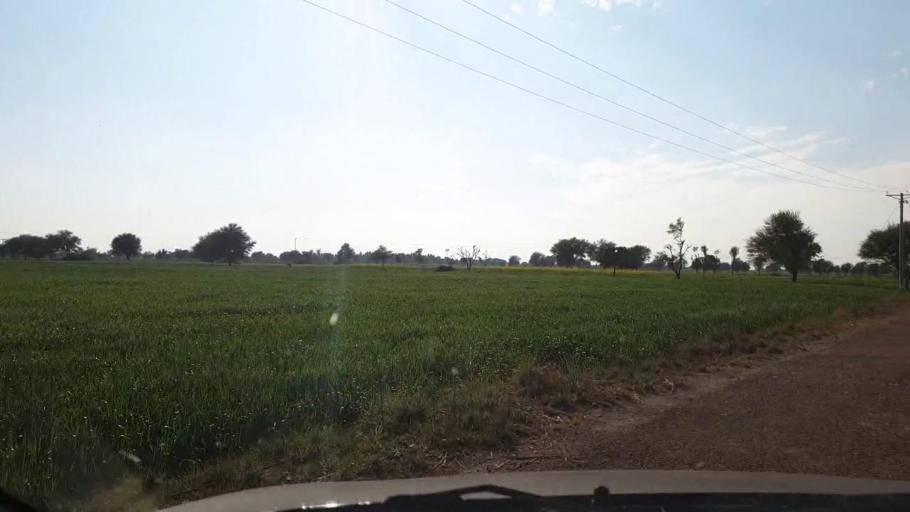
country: PK
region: Sindh
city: Sinjhoro
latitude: 25.9819
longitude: 68.8365
